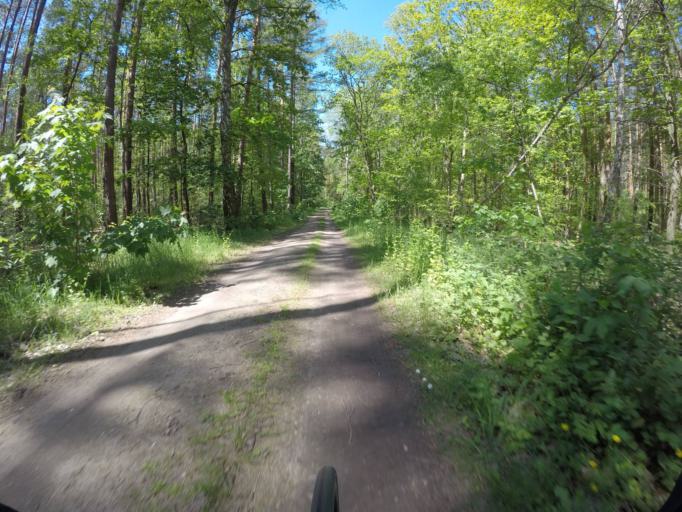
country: DE
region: Brandenburg
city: Potsdam
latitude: 52.4551
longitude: 13.0759
